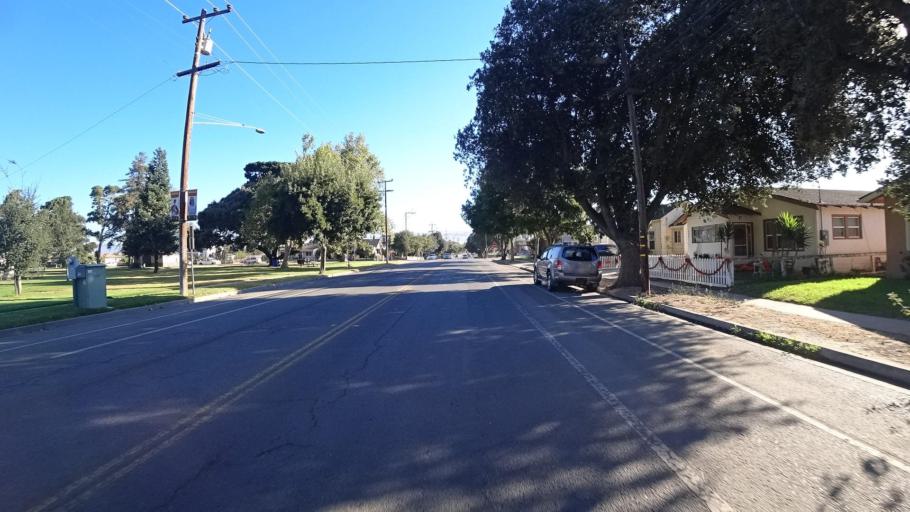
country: US
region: California
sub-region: Monterey County
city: Gonzales
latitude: 36.5091
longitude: -121.4435
